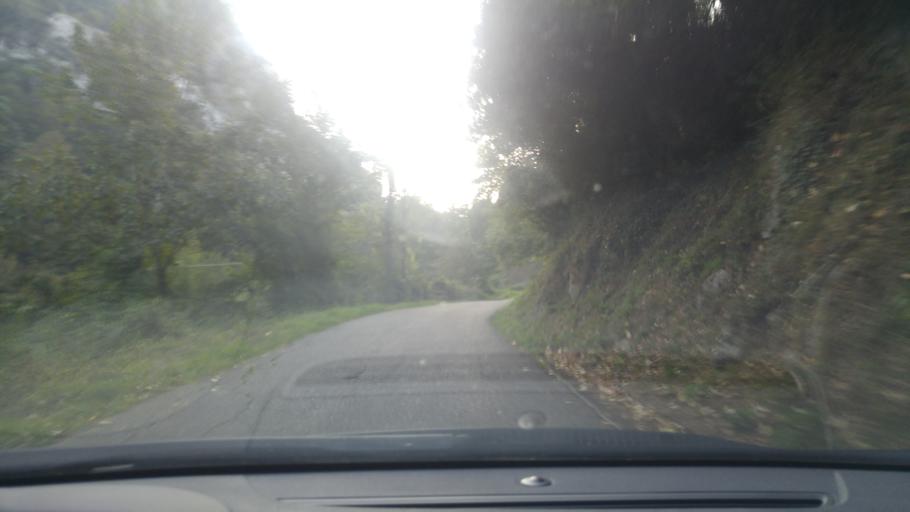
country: ES
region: Asturias
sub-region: Province of Asturias
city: Proaza
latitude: 43.2478
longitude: -6.0284
